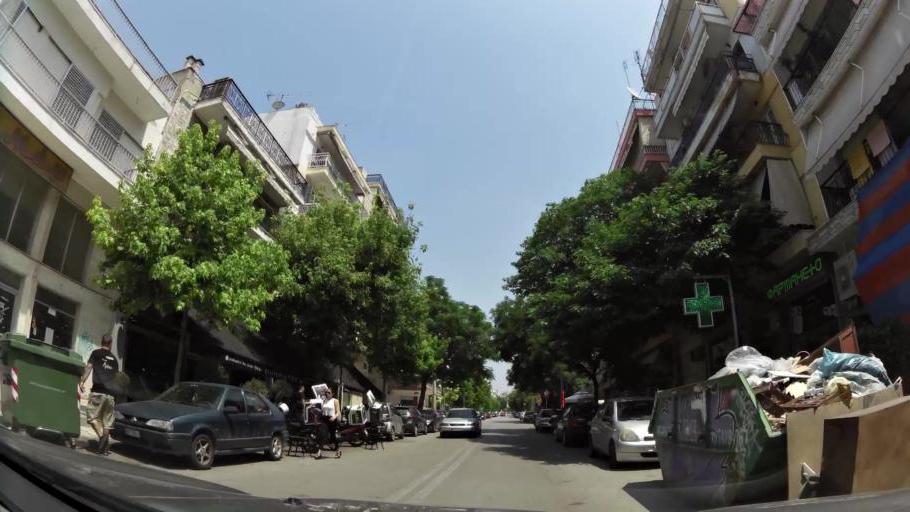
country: GR
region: Central Macedonia
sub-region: Nomos Thessalonikis
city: Menemeni
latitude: 40.6669
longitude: 22.8982
